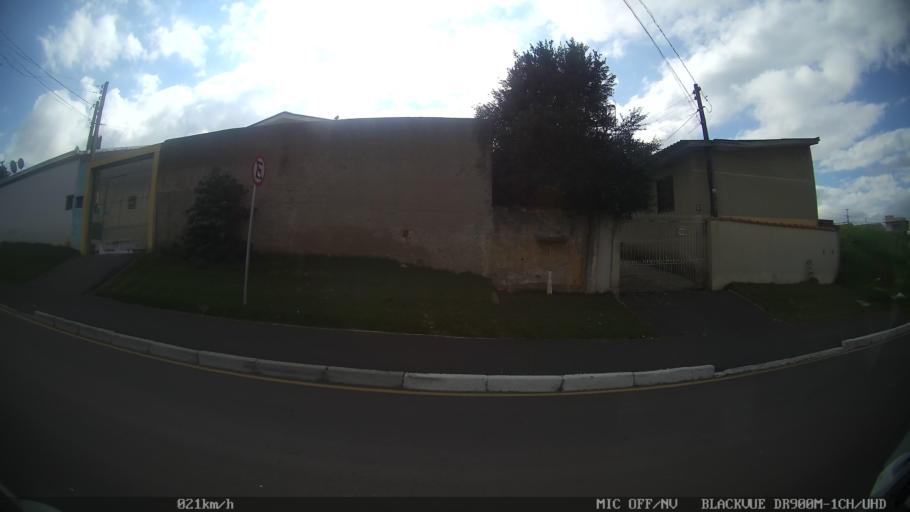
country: BR
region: Parana
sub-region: Colombo
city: Colombo
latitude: -25.3567
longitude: -49.1862
